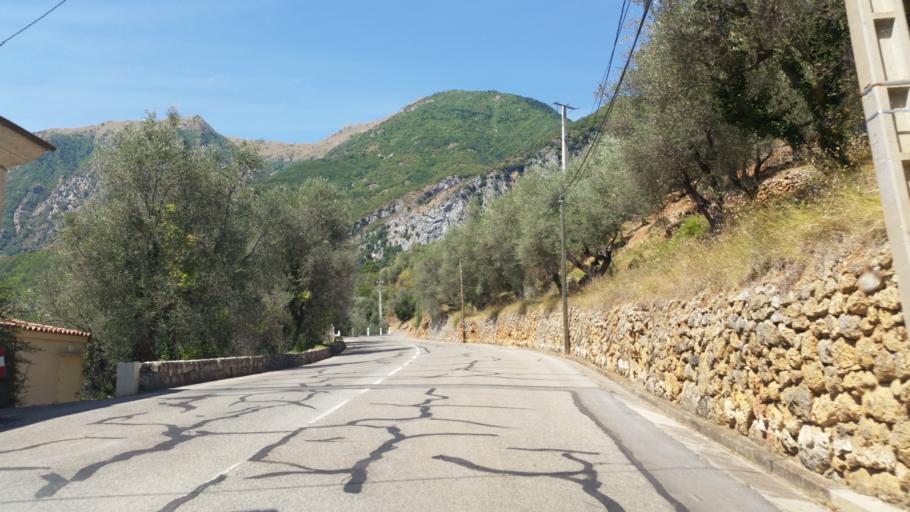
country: FR
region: Provence-Alpes-Cote d'Azur
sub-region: Departement des Alpes-Maritimes
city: Breil-sur-Roya
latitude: 43.9424
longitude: 7.5054
